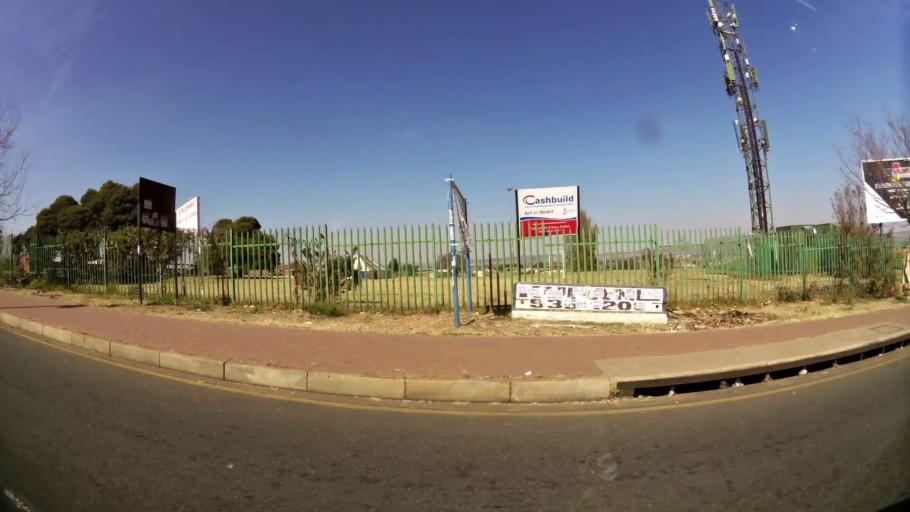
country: ZA
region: Gauteng
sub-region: City of Johannesburg Metropolitan Municipality
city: Soweto
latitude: -26.2813
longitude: 27.8596
